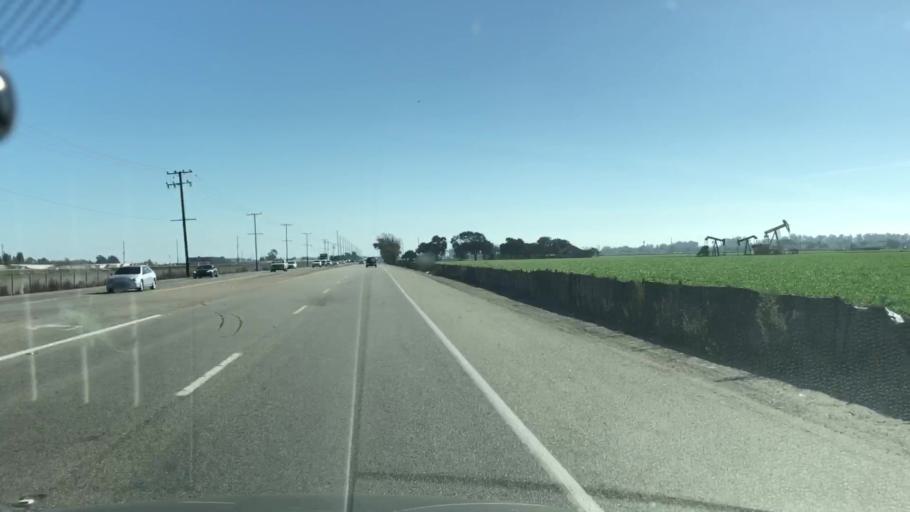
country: US
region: California
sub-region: Ventura County
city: Oxnard
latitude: 34.1875
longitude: -119.1425
